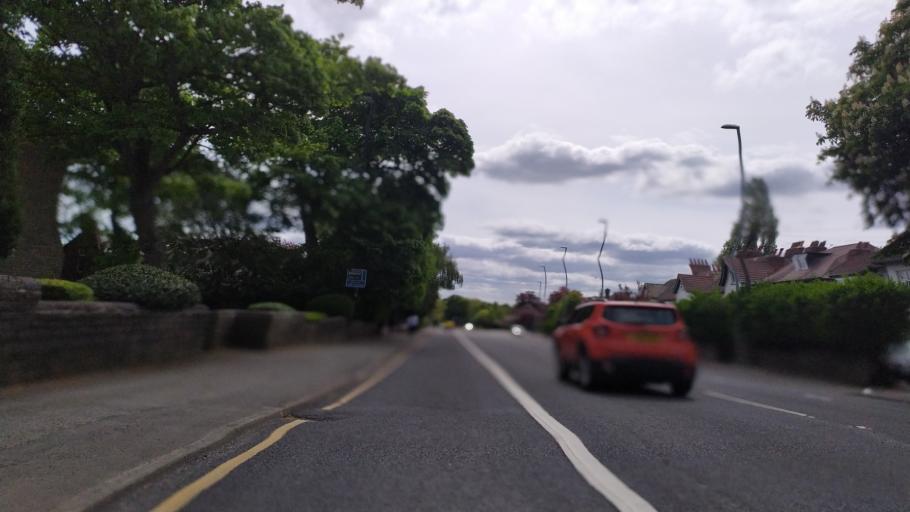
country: GB
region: England
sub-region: City and Borough of Leeds
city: Horsforth
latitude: 53.8351
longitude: -1.5932
